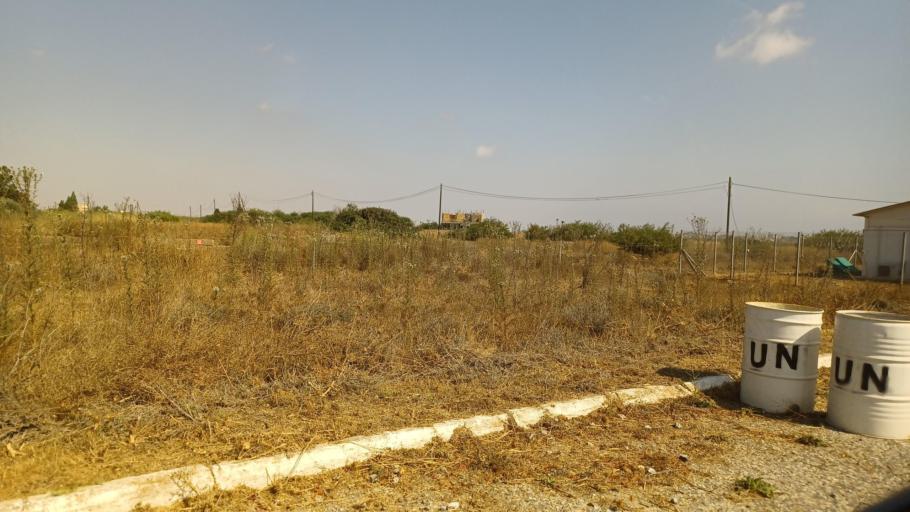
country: CY
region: Ammochostos
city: Deryneia
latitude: 35.0721
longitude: 33.9647
